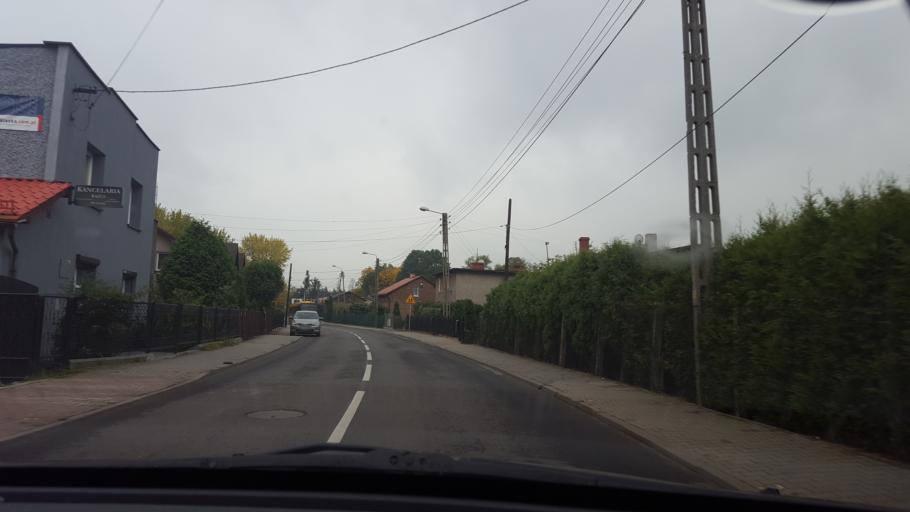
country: PL
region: Silesian Voivodeship
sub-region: Ruda Slaska
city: Ruda Slaska
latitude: 50.2345
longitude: 18.8634
